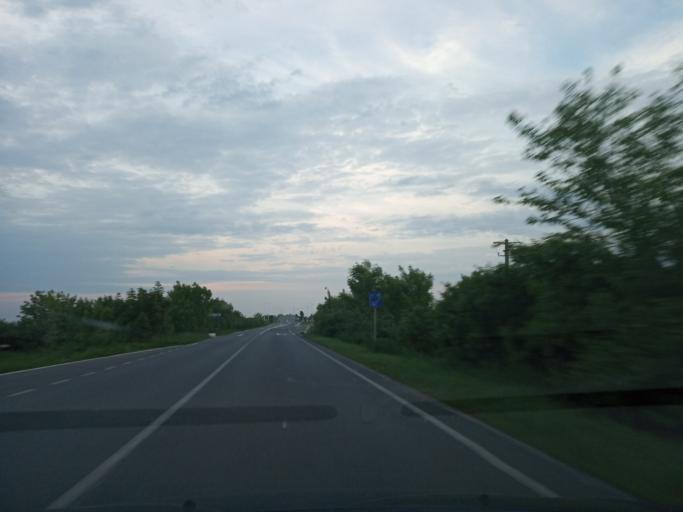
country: RO
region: Timis
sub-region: Comuna Voiteg
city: Voiteg
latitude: 45.4577
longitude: 21.2348
